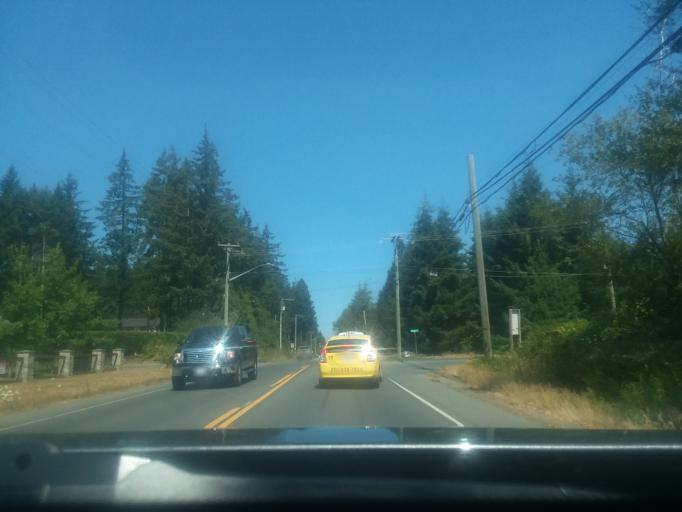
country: CA
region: British Columbia
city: Courtenay
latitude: 49.7006
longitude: -124.9343
